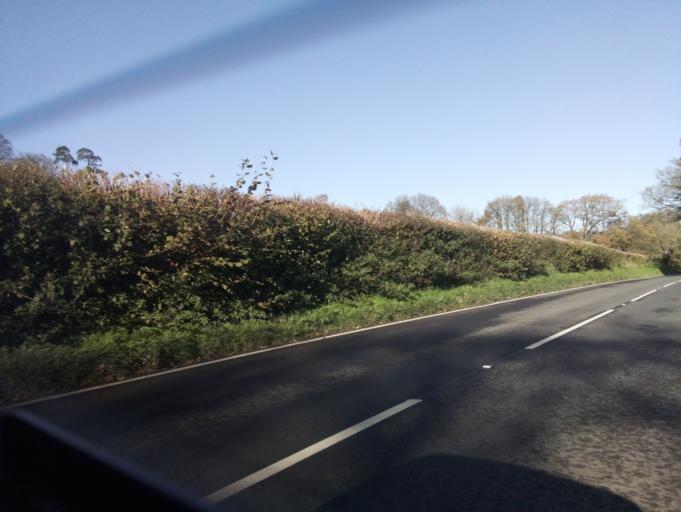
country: GB
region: England
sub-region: Dorset
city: Dorchester
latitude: 50.8247
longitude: -2.4808
